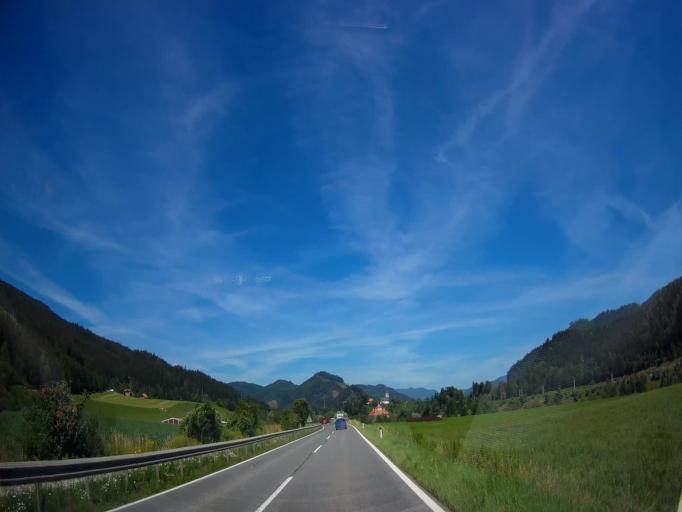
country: AT
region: Carinthia
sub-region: Politischer Bezirk Sankt Veit an der Glan
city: Althofen
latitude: 46.8842
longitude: 14.4445
